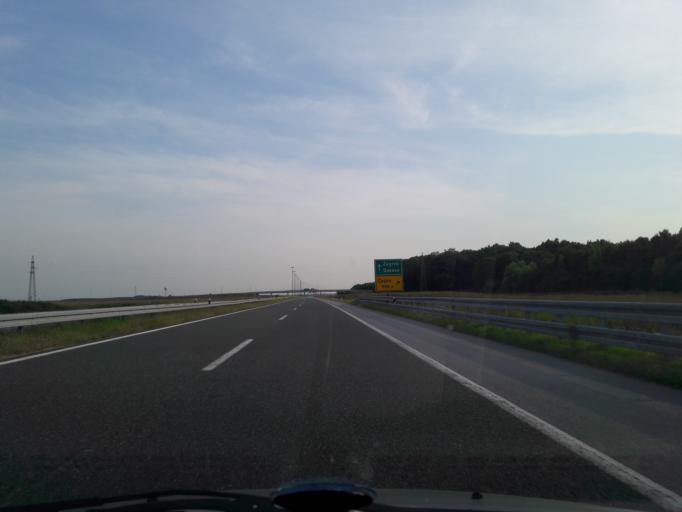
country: HR
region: Osjecko-Baranjska
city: Cepin
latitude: 45.5104
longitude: 18.5066
